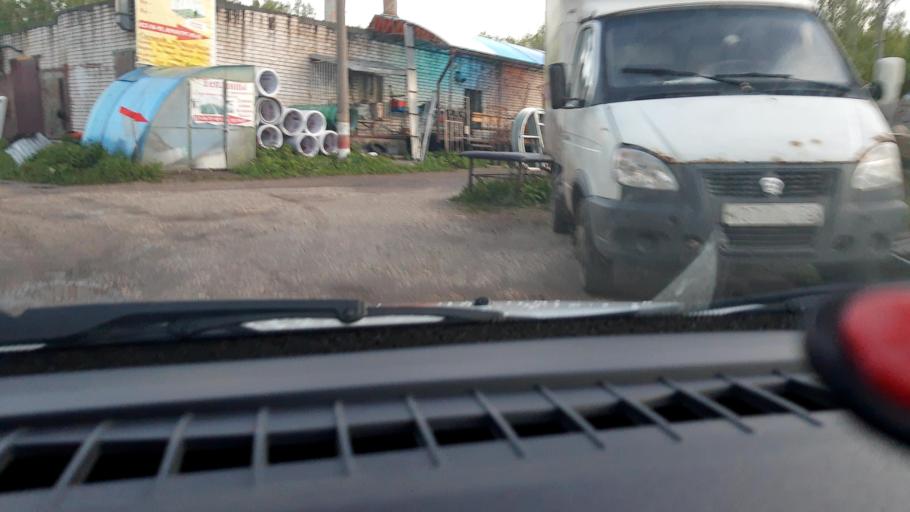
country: RU
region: Nizjnij Novgorod
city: Afonino
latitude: 56.2283
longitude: 44.0869
